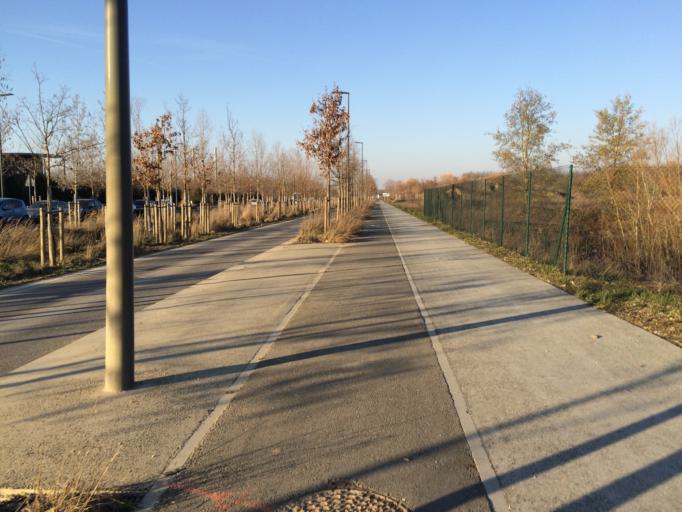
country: FR
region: Ile-de-France
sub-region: Departement de l'Essonne
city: Vauhallan
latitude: 48.7157
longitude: 2.2027
